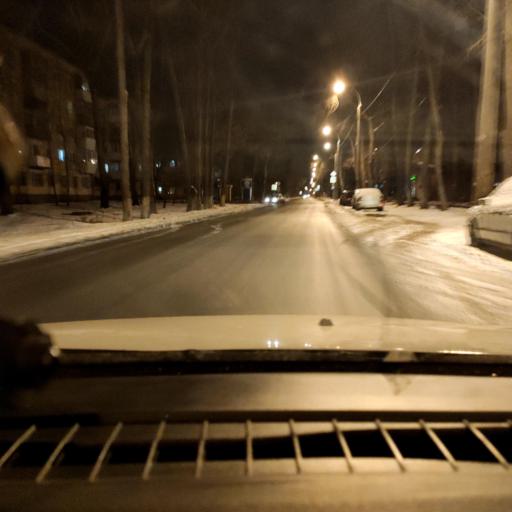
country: RU
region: Samara
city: Samara
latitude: 53.1164
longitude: 50.0697
